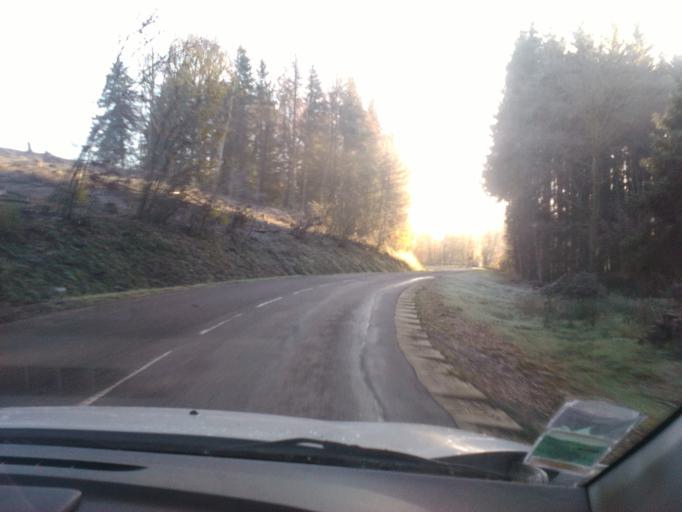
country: FR
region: Lorraine
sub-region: Departement des Vosges
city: Uzemain
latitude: 48.0570
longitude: 6.3568
